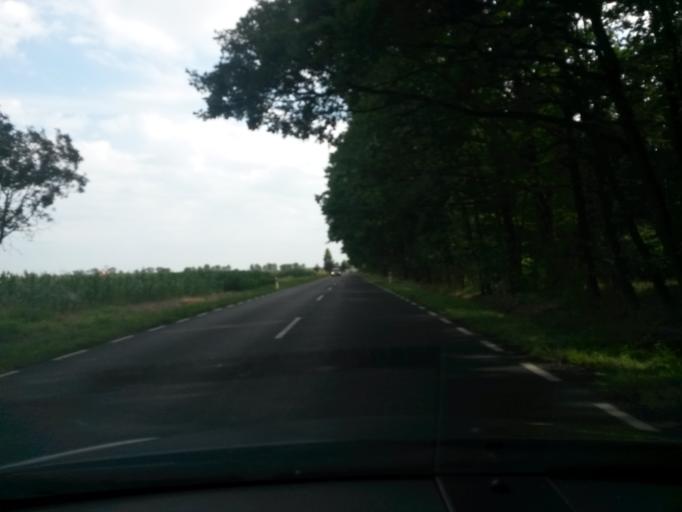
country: PL
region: Greater Poland Voivodeship
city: Miejska Gorka
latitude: 51.6586
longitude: 16.9299
